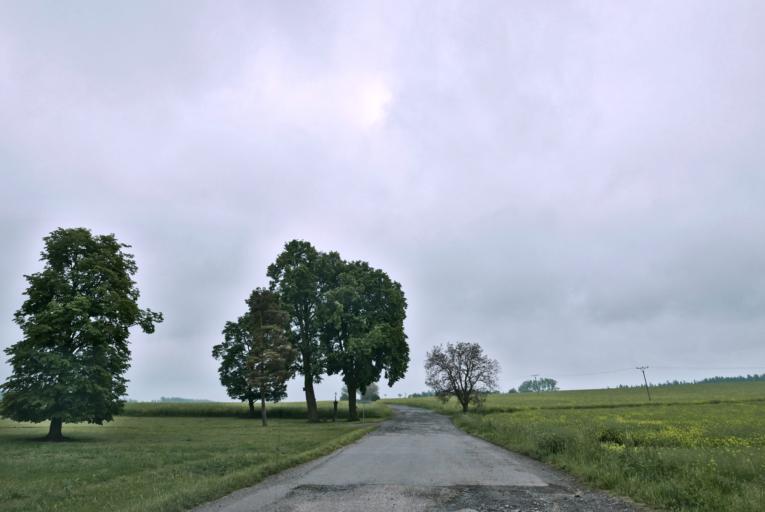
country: CZ
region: Plzensky
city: Zihle
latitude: 50.0222
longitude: 13.3274
